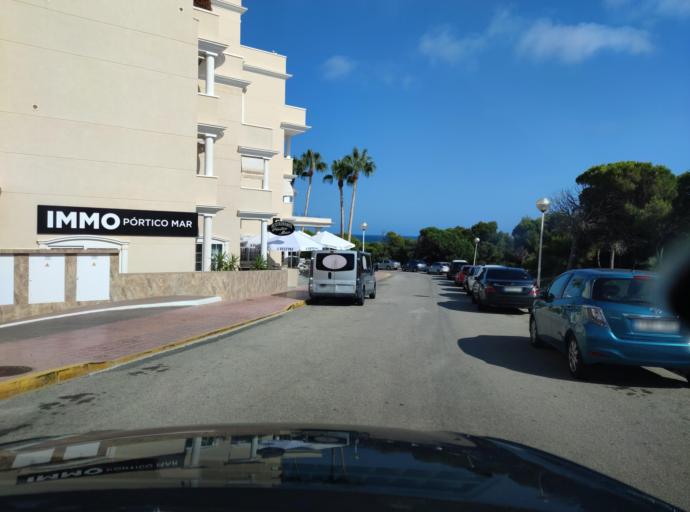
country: ES
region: Valencia
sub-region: Provincia de Alicante
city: Guardamar del Segura
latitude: 38.0624
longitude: -0.6548
